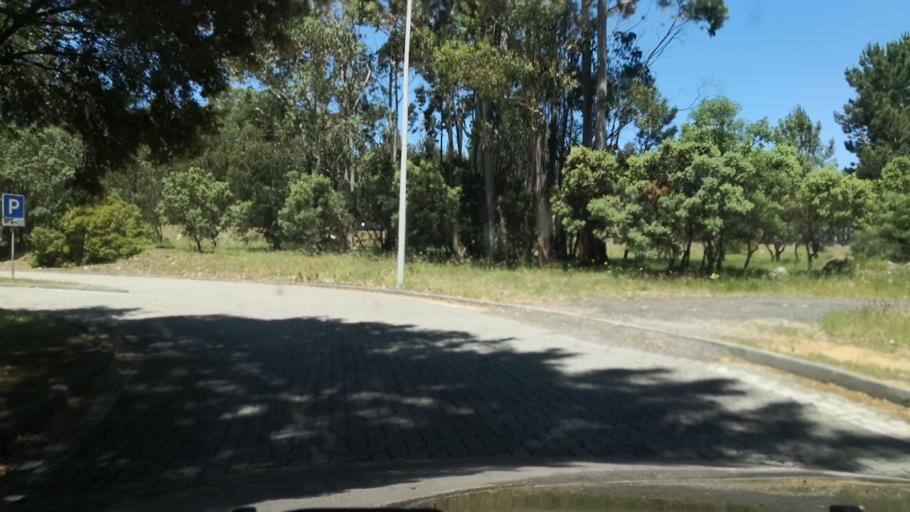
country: PT
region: Santarem
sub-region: Ourem
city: Fatima
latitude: 39.5549
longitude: -8.6530
